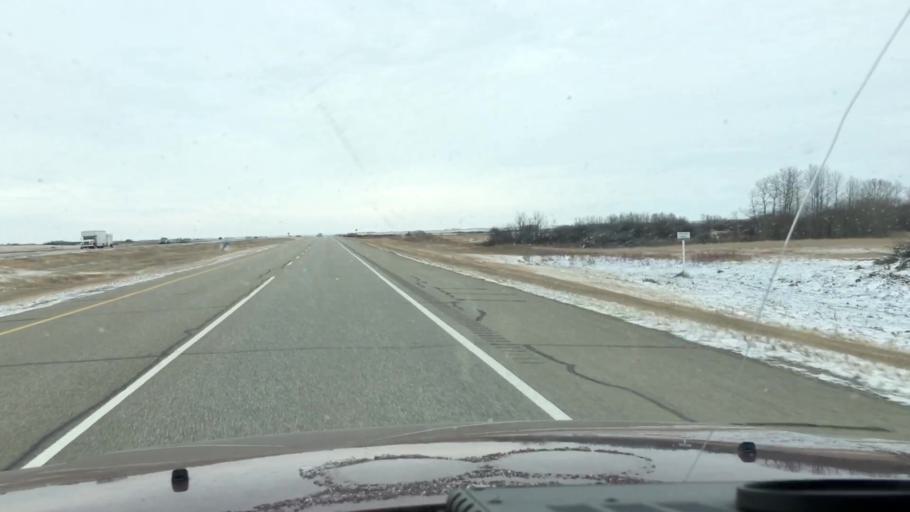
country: CA
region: Saskatchewan
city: Watrous
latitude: 51.3579
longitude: -106.1245
